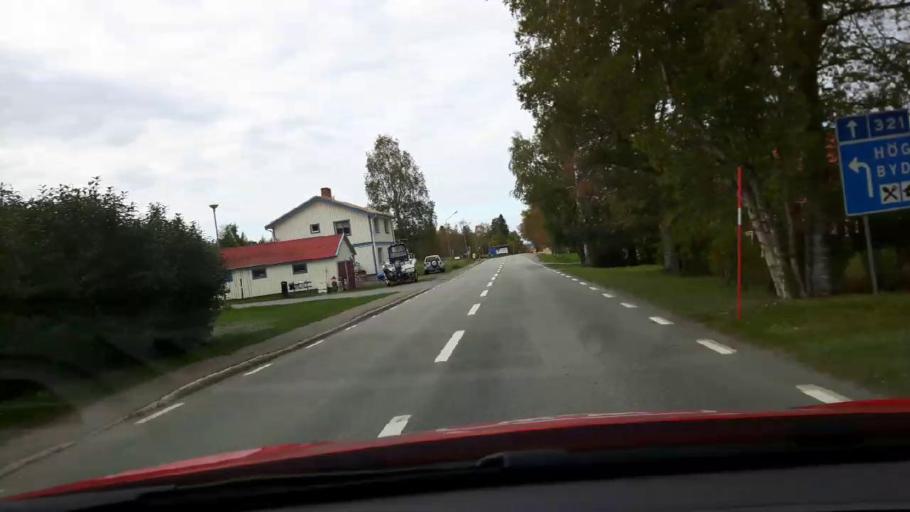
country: SE
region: Jaemtland
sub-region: Krokoms Kommun
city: Krokom
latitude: 63.1768
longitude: 14.0924
